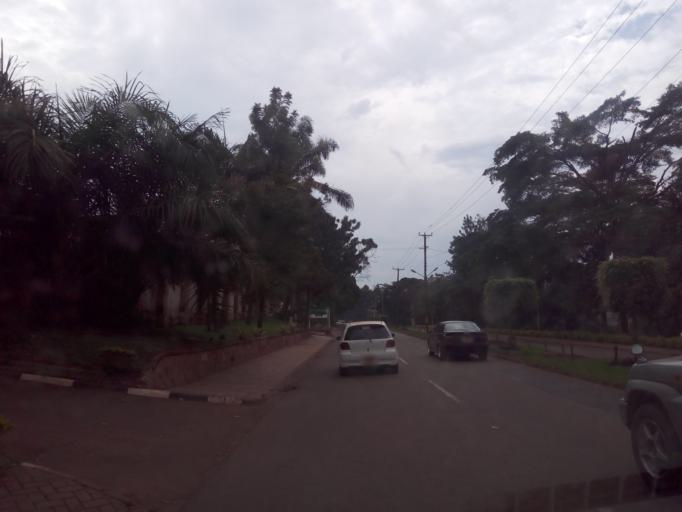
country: UG
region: Central Region
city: Kampala Central Division
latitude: 0.3279
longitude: 32.5835
